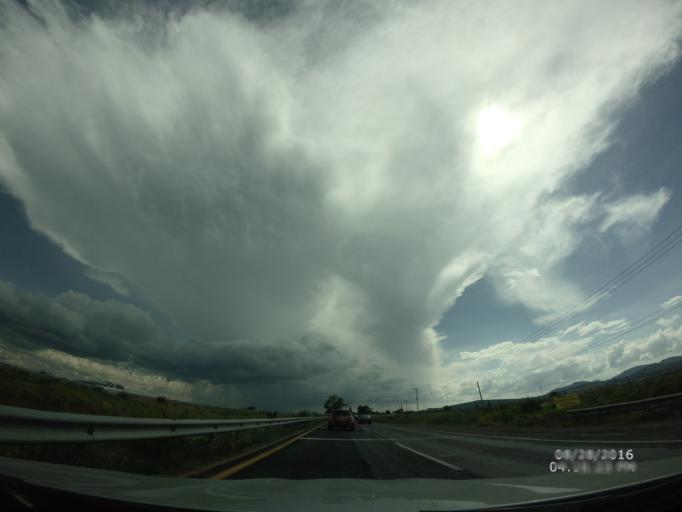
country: MX
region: Hidalgo
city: Zapotlan de Juarez
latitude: 19.9872
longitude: -98.8421
